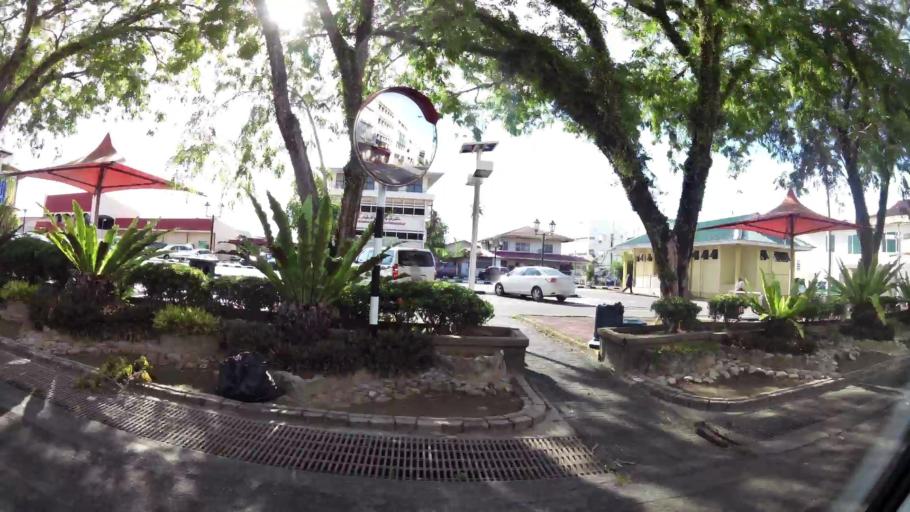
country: BN
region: Belait
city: Kuala Belait
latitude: 4.5831
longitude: 114.1909
